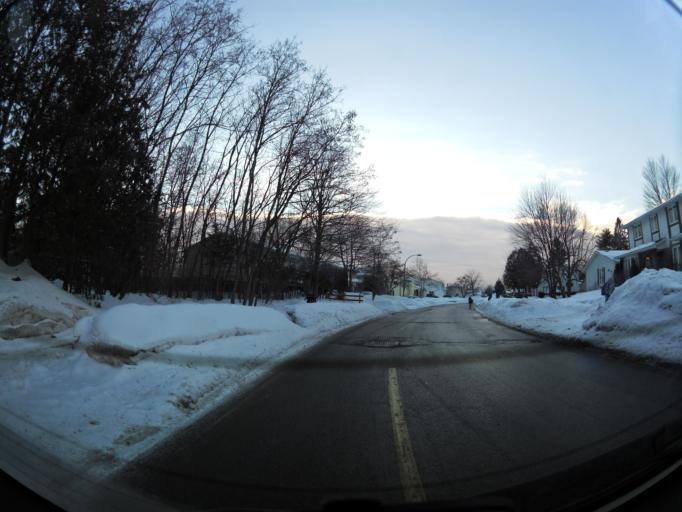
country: CA
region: Ontario
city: Ottawa
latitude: 45.4357
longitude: -75.5636
